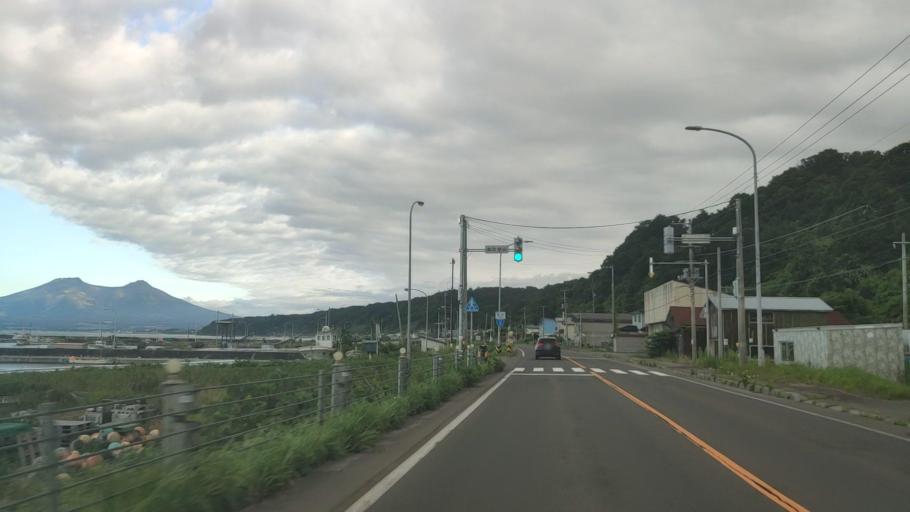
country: JP
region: Hokkaido
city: Nanae
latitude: 42.1351
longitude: 140.5078
